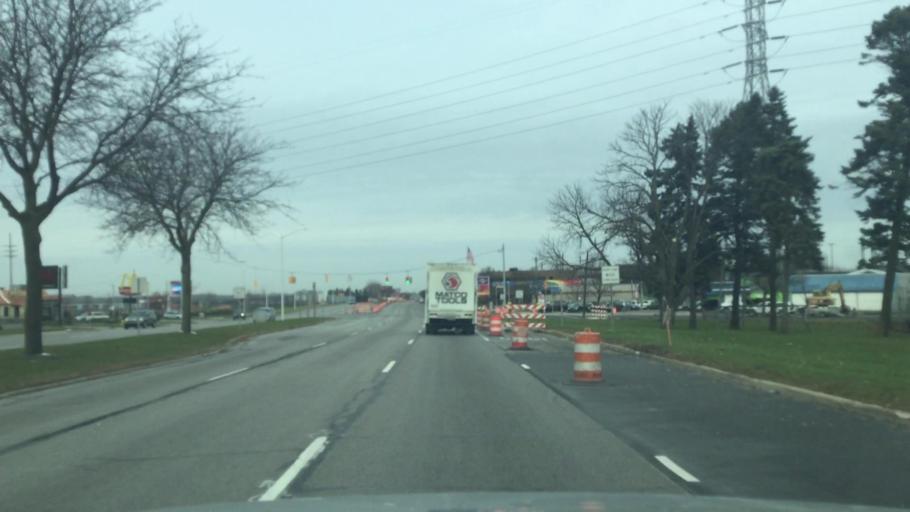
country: US
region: Michigan
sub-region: Oakland County
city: Pontiac
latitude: 42.6186
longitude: -83.2780
